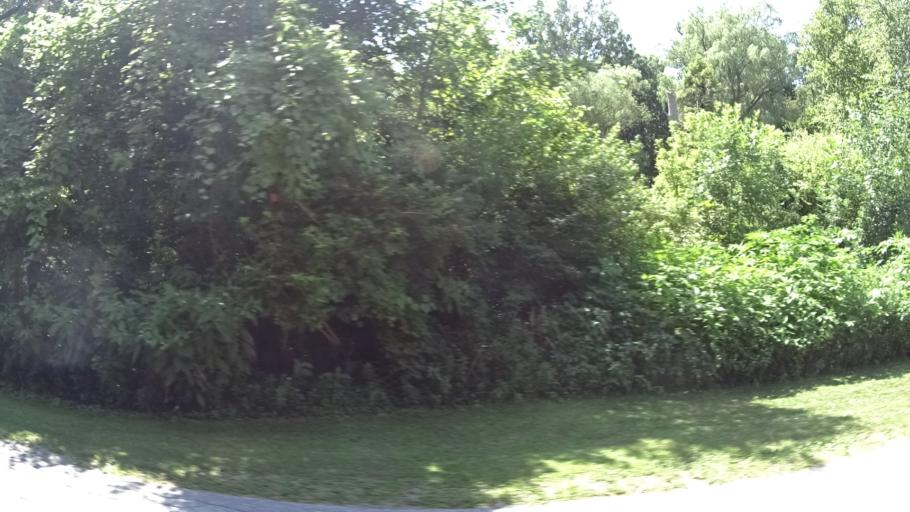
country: US
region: Ohio
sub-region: Erie County
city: Sandusky
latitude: 41.4188
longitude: -82.8054
